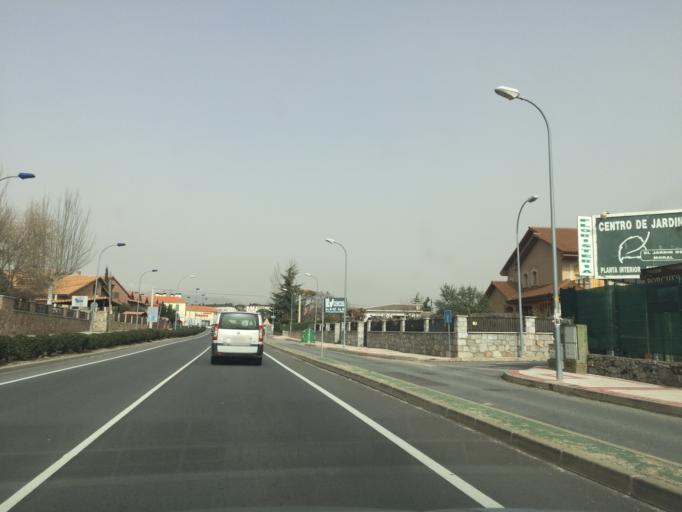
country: ES
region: Madrid
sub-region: Provincia de Madrid
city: Moralzarzal
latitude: 40.6701
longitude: -3.9743
